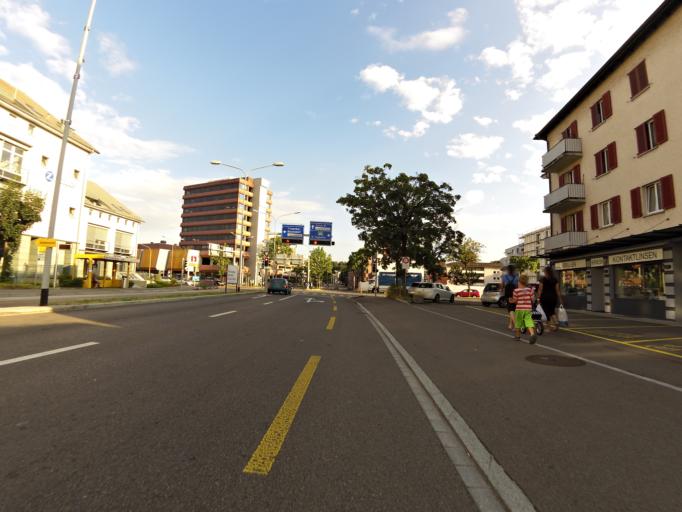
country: CH
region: Zurich
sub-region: Bezirk Buelach
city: Kloten / Horainli
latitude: 47.4540
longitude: 8.5799
